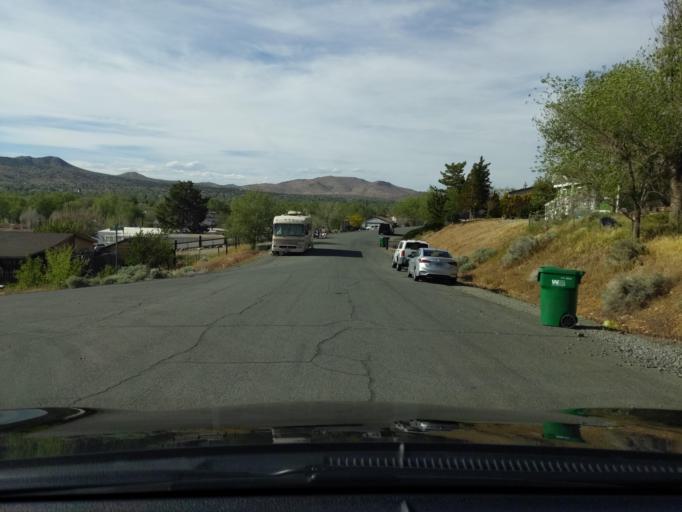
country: US
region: Nevada
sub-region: Washoe County
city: Sun Valley
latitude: 39.5835
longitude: -119.7717
